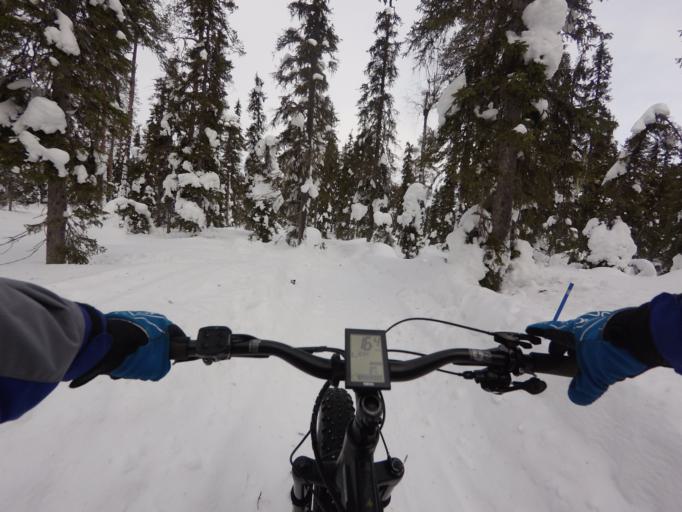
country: FI
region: Lapland
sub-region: Tunturi-Lappi
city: Kolari
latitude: 67.5986
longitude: 24.2992
